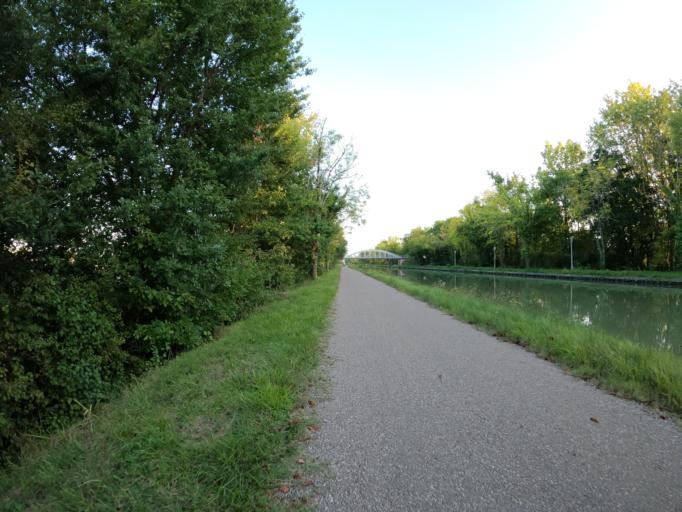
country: FR
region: Midi-Pyrenees
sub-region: Departement du Tarn-et-Garonne
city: Saint-Porquier
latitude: 43.9911
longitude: 1.2019
